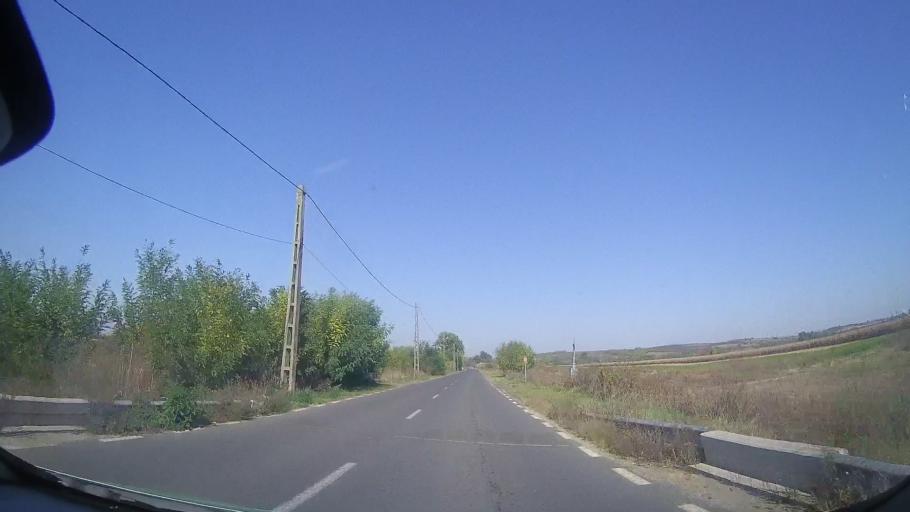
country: RO
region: Timis
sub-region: Comuna Balint
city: Balint
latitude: 45.8045
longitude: 21.8615
